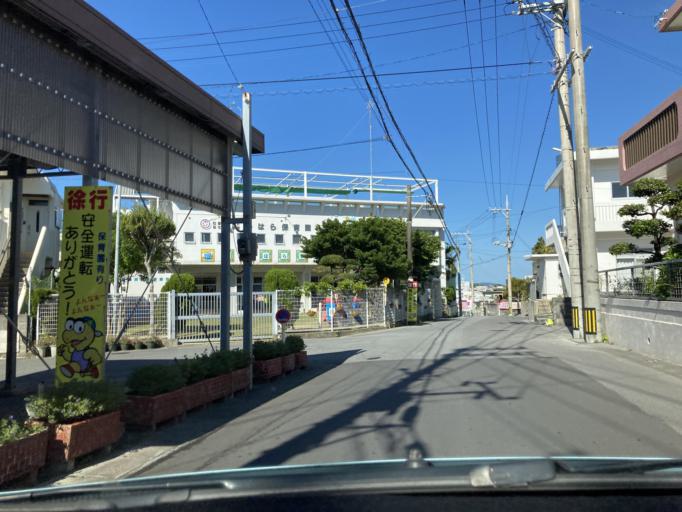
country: JP
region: Okinawa
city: Okinawa
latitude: 26.3457
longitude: 127.8290
